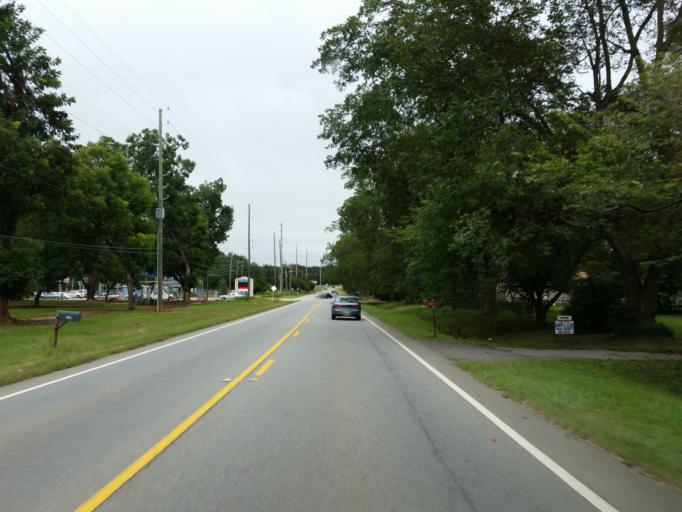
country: US
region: Georgia
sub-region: Peach County
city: Fort Valley
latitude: 32.5746
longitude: -83.9011
